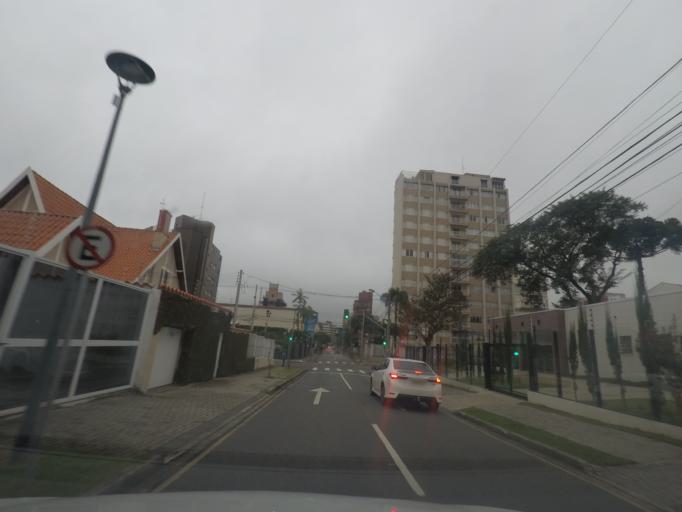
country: BR
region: Parana
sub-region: Curitiba
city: Curitiba
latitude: -25.4230
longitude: -49.2576
